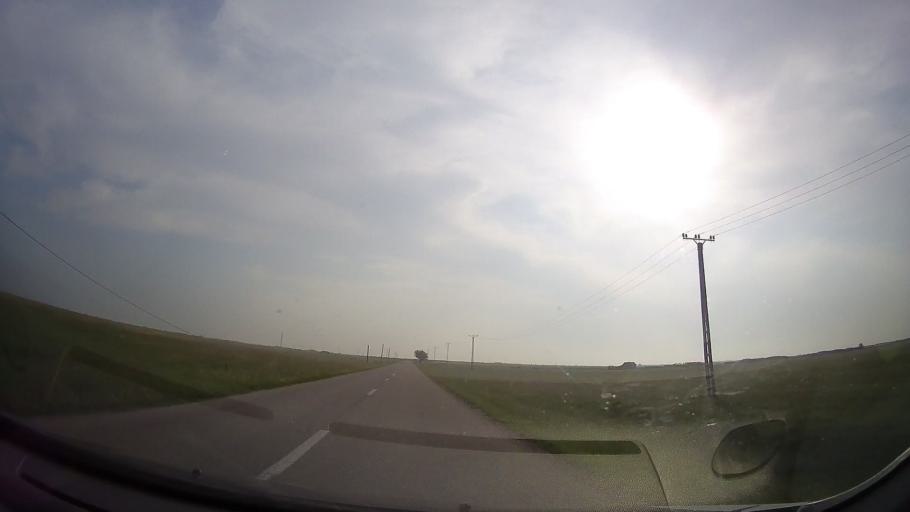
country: RO
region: Timis
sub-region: Comuna Foeni
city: Foeni
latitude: 45.5078
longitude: 20.8860
